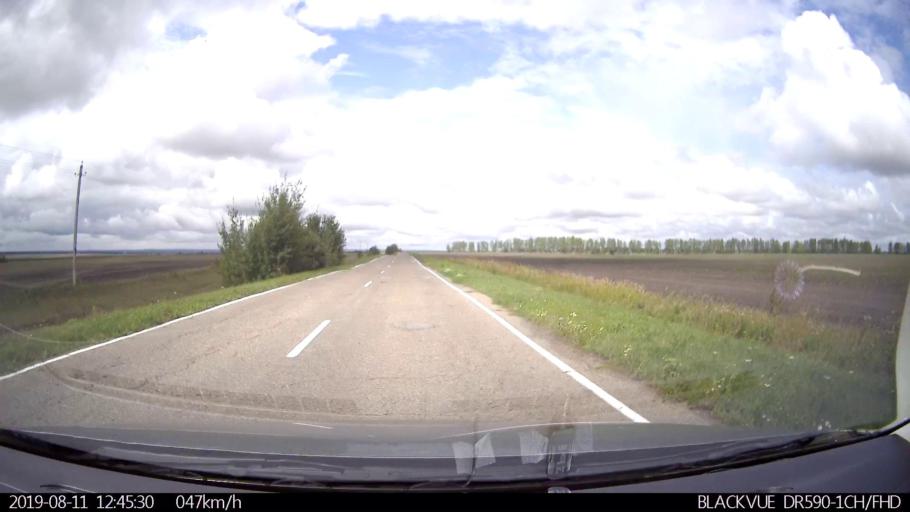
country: RU
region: Ulyanovsk
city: Ignatovka
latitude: 53.8597
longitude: 47.7275
